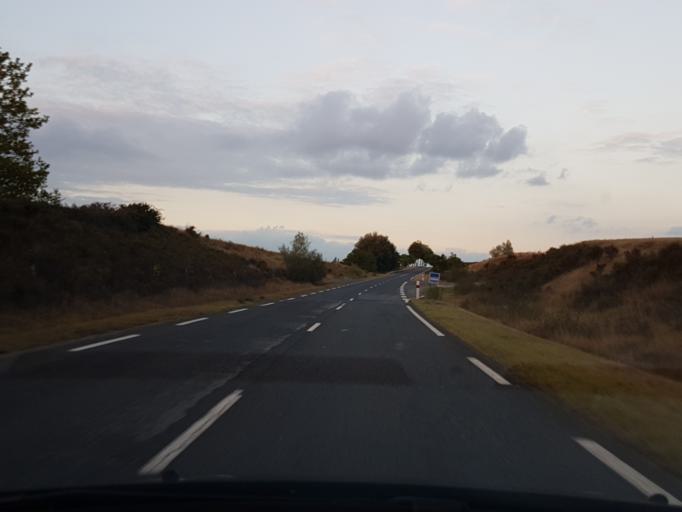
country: FR
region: Languedoc-Roussillon
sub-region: Departement de l'Aude
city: Saint-Martin-Lalande
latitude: 43.1702
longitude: 2.0004
